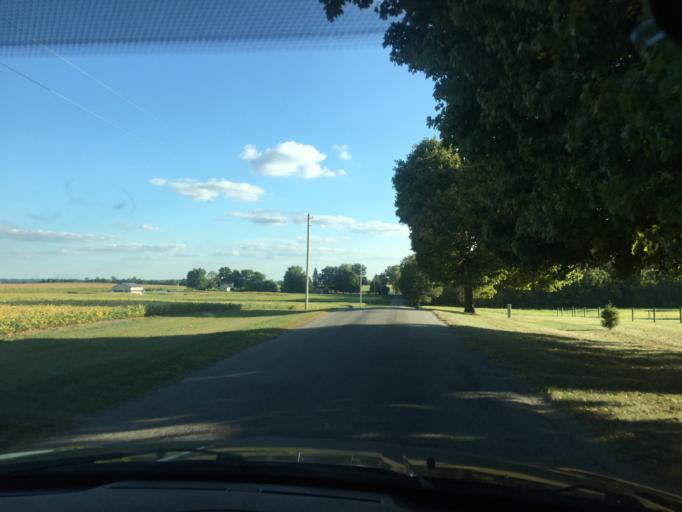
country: US
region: Ohio
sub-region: Champaign County
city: Urbana
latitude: 40.1753
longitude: -83.7634
